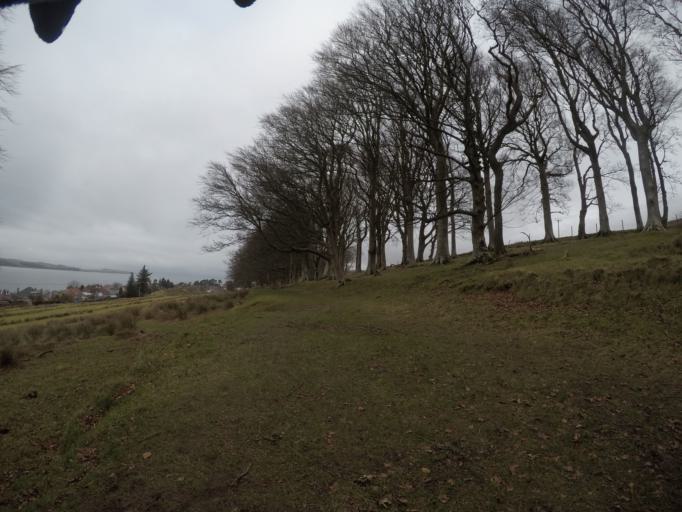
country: GB
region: Scotland
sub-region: North Ayrshire
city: Fairlie
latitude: 55.7551
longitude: -4.8491
